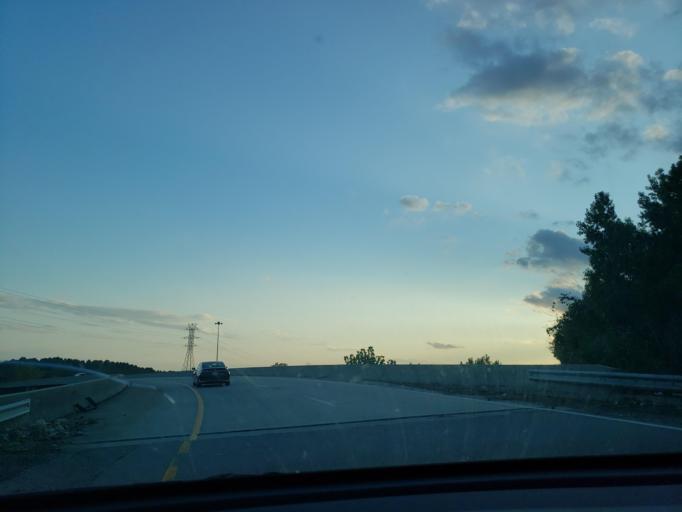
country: US
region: North Carolina
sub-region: Durham County
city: Durham
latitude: 36.0145
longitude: -78.8698
